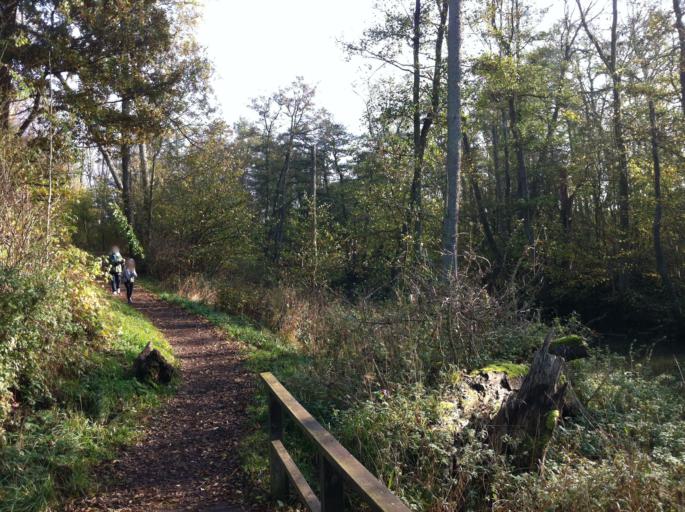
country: SE
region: Skane
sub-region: Helsingborg
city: Gantofta
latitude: 55.9998
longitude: 12.7737
